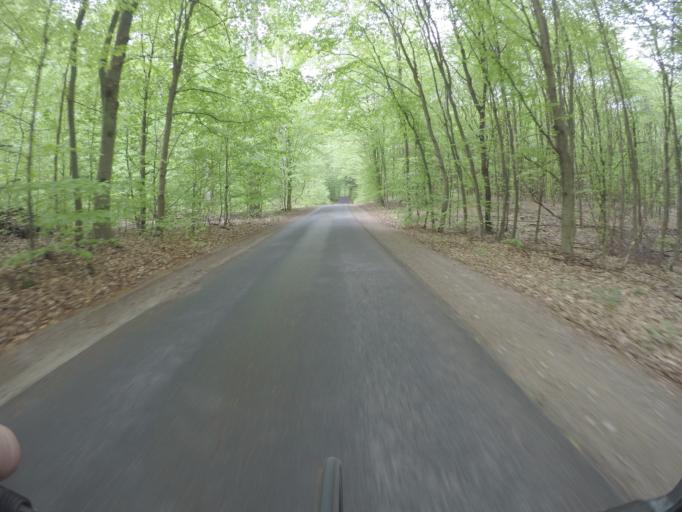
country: DE
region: Brandenburg
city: Marienwerder
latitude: 52.8998
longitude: 13.6664
